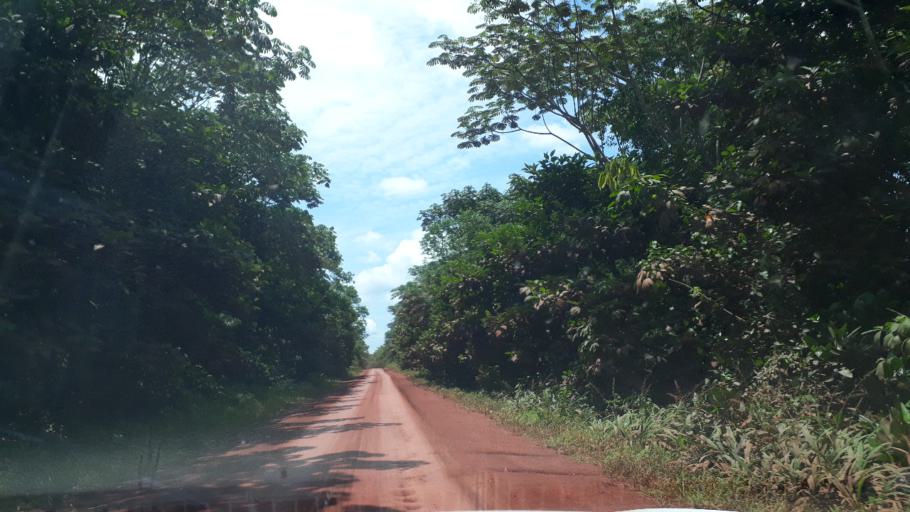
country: CD
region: Eastern Province
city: Kisangani
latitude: 0.5401
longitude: 25.8246
